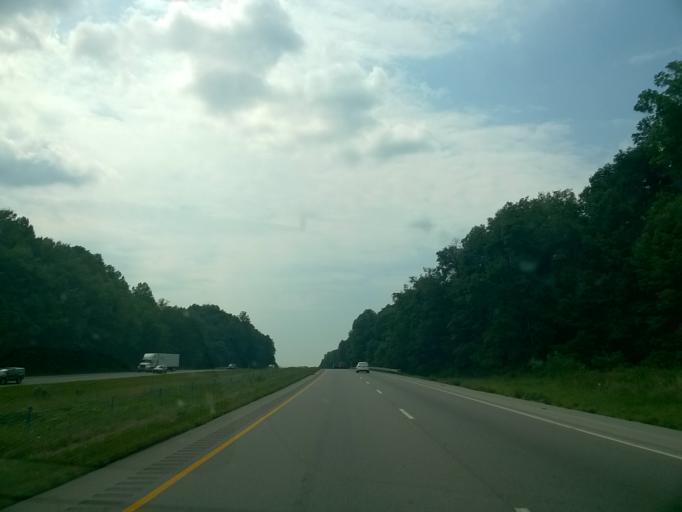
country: US
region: Indiana
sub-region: Putnam County
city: Cloverdale
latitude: 39.5115
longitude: -86.9310
